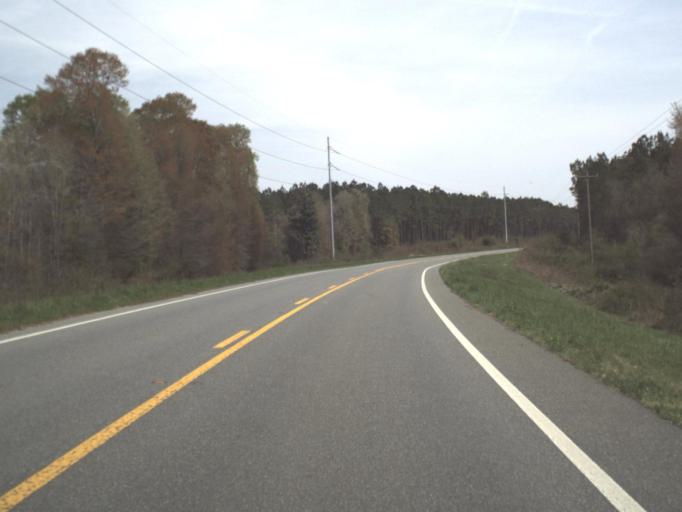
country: US
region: Alabama
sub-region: Houston County
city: Cottonwood
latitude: 30.9486
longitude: -85.3636
